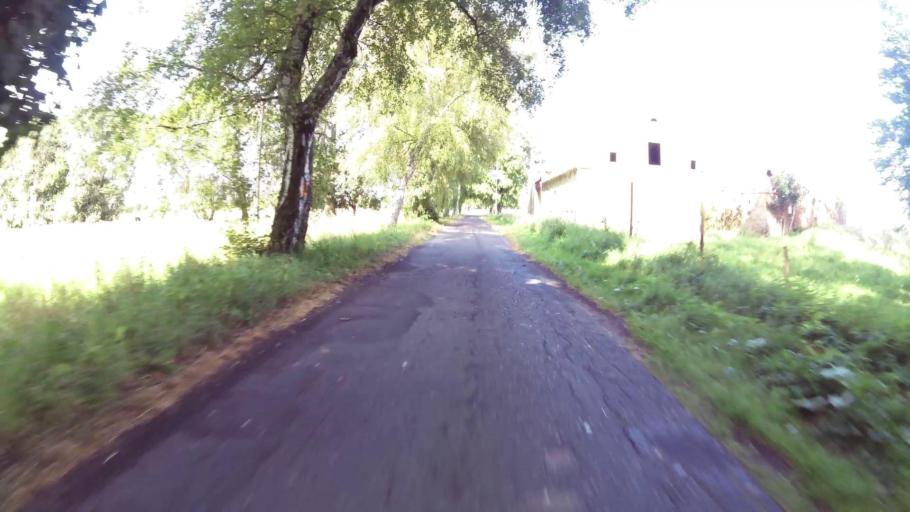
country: PL
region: West Pomeranian Voivodeship
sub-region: Powiat stargardzki
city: Suchan
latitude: 53.2899
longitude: 15.3635
